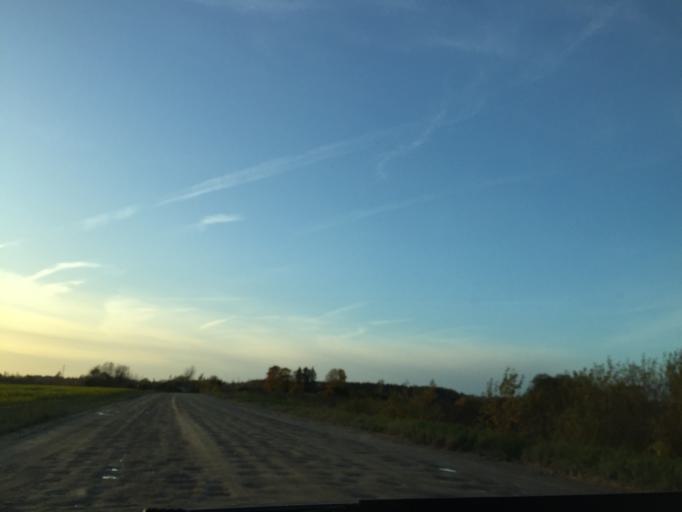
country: LV
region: Malpils
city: Malpils
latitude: 56.8920
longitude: 24.9401
